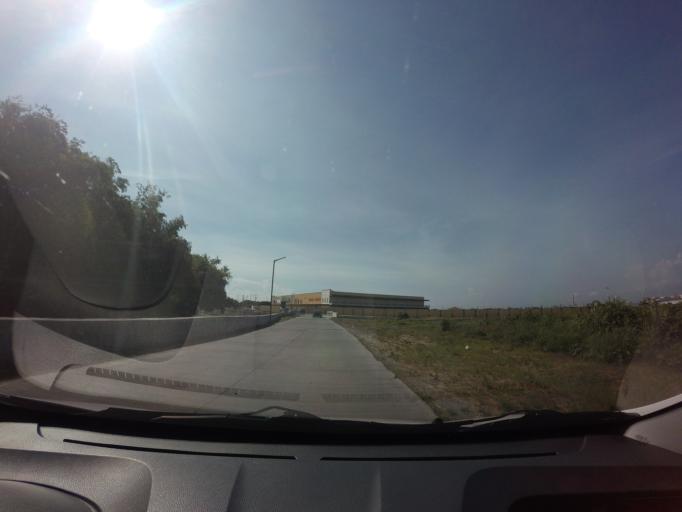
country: PH
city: Sambayanihan People's Village
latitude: 14.4745
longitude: 120.9853
